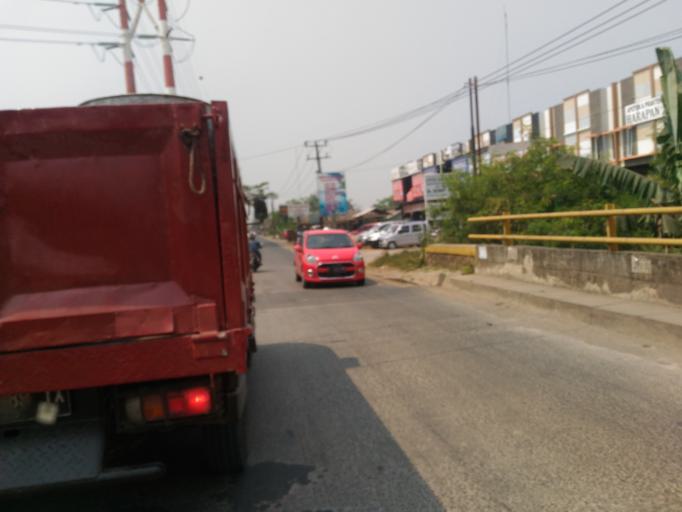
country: ID
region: West Java
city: Sepatan
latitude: -6.1477
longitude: 106.5775
